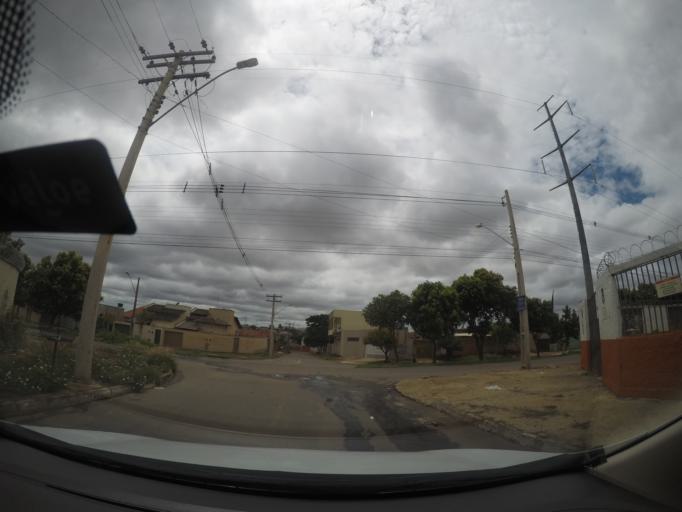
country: BR
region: Goias
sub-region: Goiania
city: Goiania
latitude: -16.7322
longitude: -49.3587
